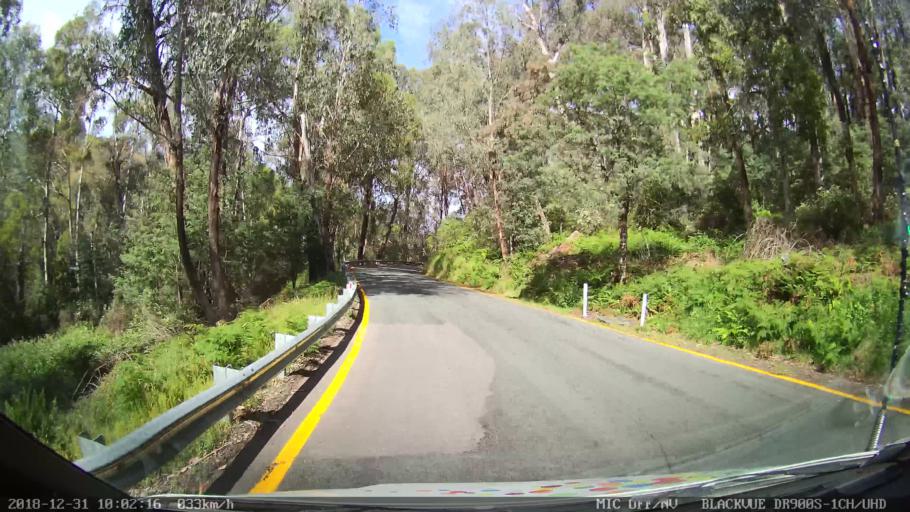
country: AU
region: New South Wales
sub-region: Snowy River
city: Jindabyne
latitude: -36.5307
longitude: 148.1997
